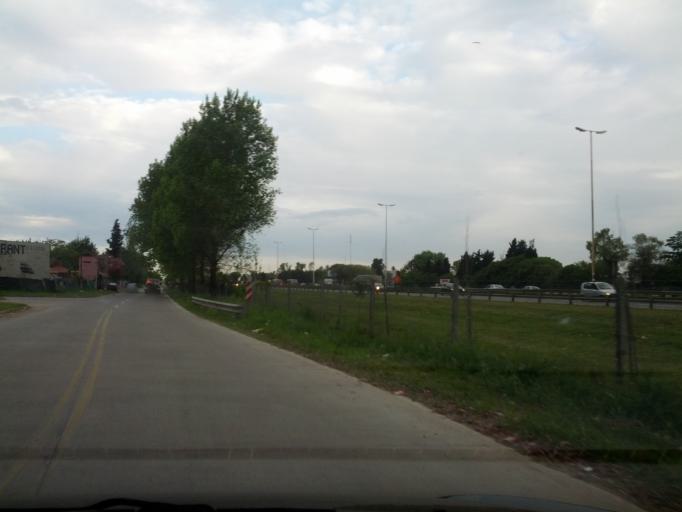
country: AR
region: Buenos Aires
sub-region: Partido de General Rodriguez
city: General Rodriguez
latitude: -34.6165
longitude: -58.8471
